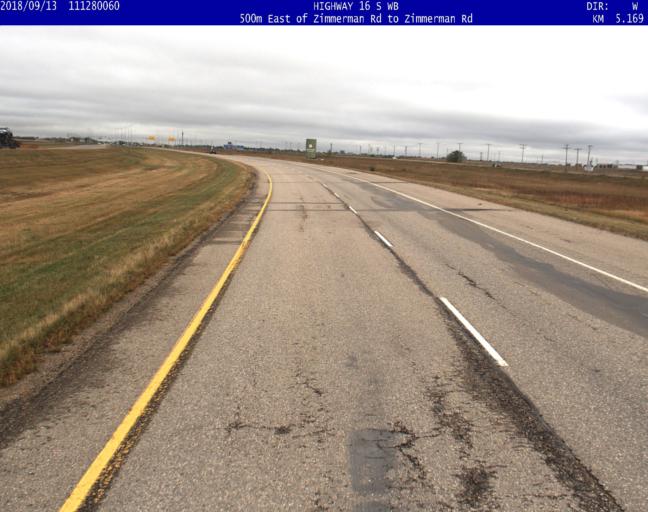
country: CA
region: Saskatchewan
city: Saskatoon
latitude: 52.0859
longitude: -106.5232
